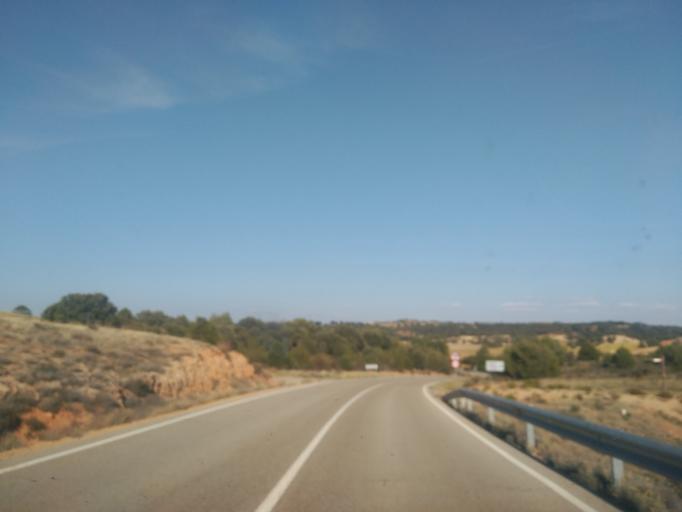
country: ES
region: Castille and Leon
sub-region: Provincia de Soria
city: Alcubilla de Avellaneda
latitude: 41.7286
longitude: -3.3036
